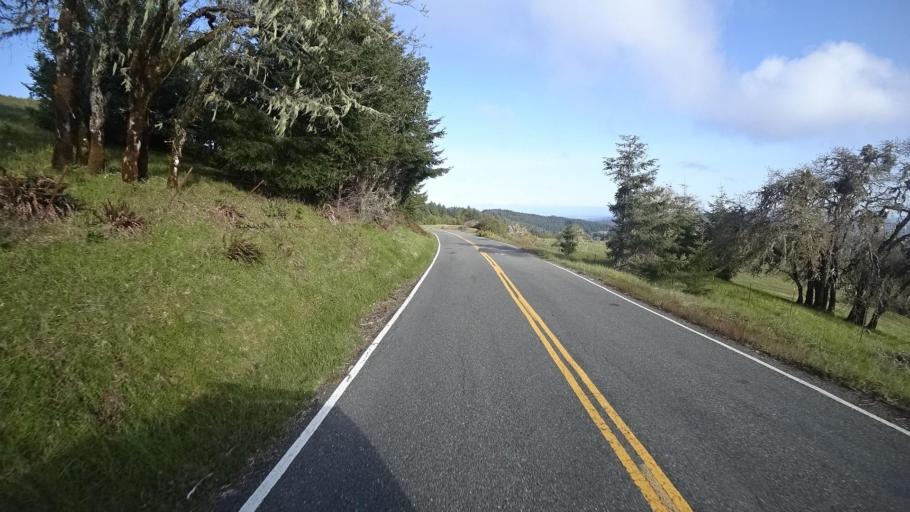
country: US
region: California
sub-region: Humboldt County
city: Blue Lake
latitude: 40.7376
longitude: -123.9466
